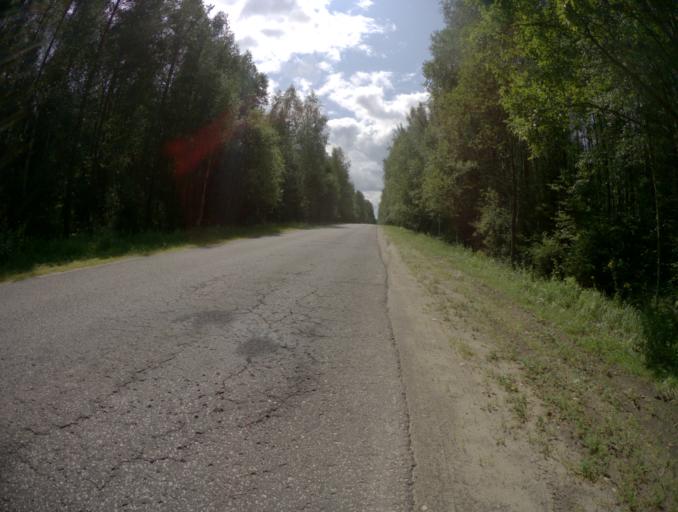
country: RU
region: Vladimir
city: Raduzhnyy
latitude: 55.9760
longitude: 40.2459
